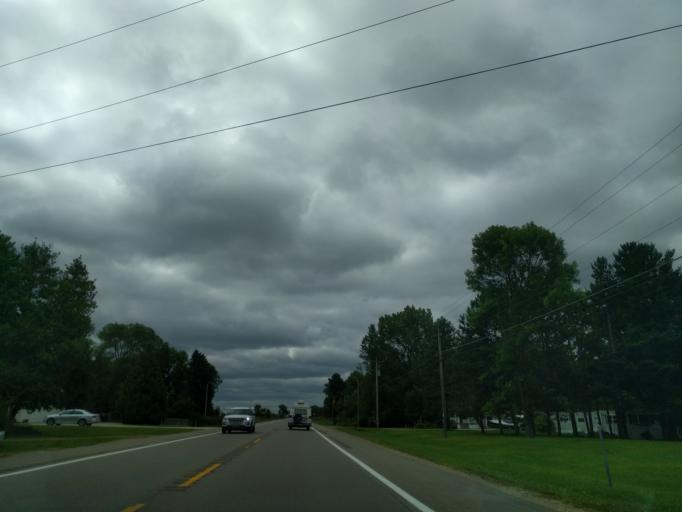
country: US
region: Michigan
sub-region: Menominee County
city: Menominee
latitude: 45.2016
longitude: -87.5372
